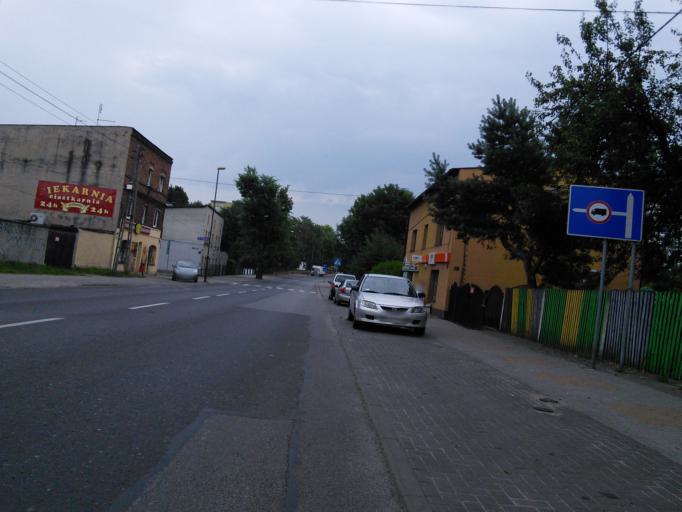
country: PL
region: Silesian Voivodeship
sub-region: Piekary Slaskie
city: Brzeziny Slaskie
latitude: 50.3685
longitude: 18.9761
